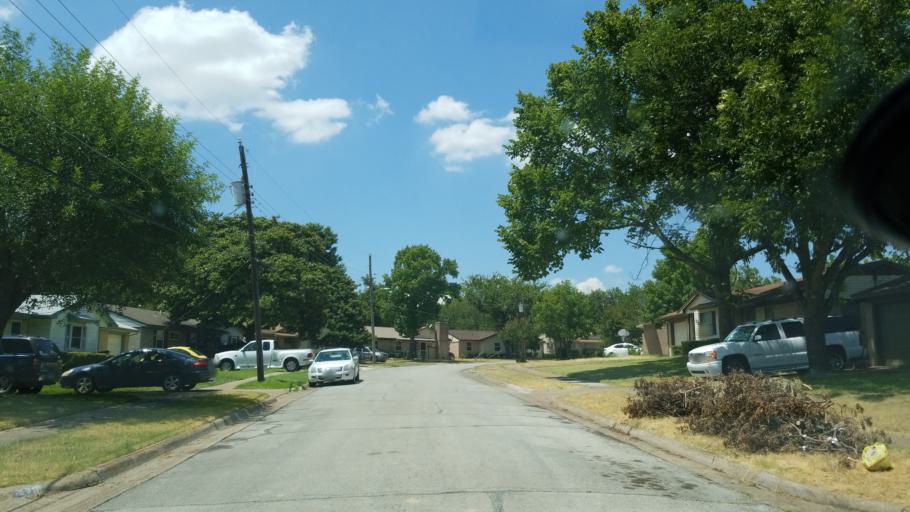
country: US
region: Texas
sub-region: Dallas County
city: Duncanville
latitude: 32.6696
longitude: -96.8995
